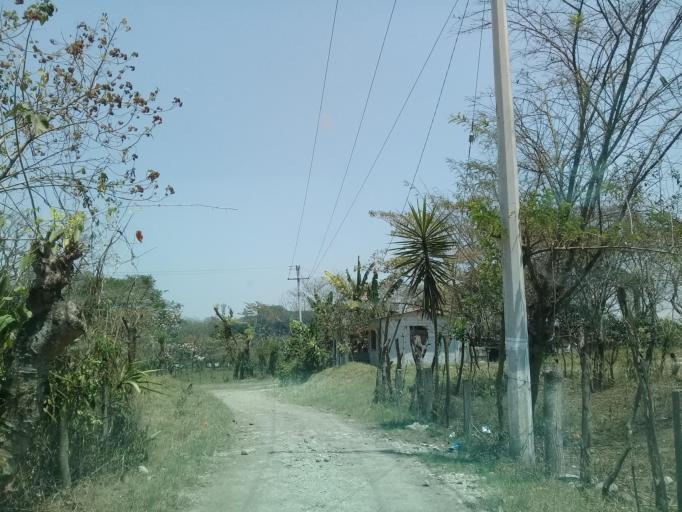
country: MX
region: Veracruz
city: Paraje Nuevo
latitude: 18.8713
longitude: -96.8657
